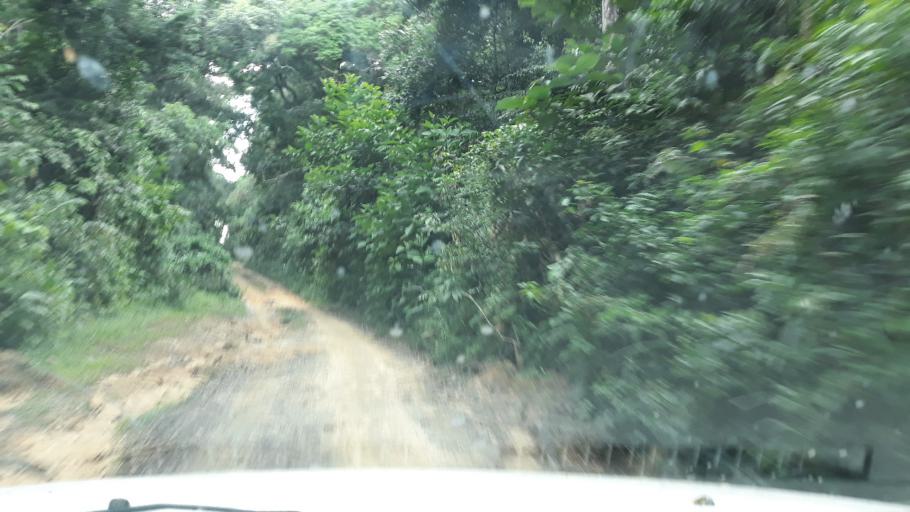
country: CD
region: Maniema
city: Kampene
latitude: -2.7319
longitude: 26.8847
